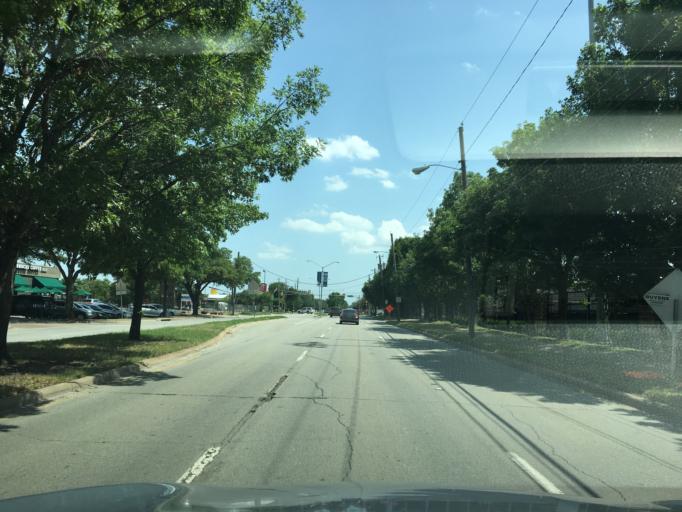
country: US
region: Texas
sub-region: Dallas County
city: Addison
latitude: 32.9160
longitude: -96.8185
